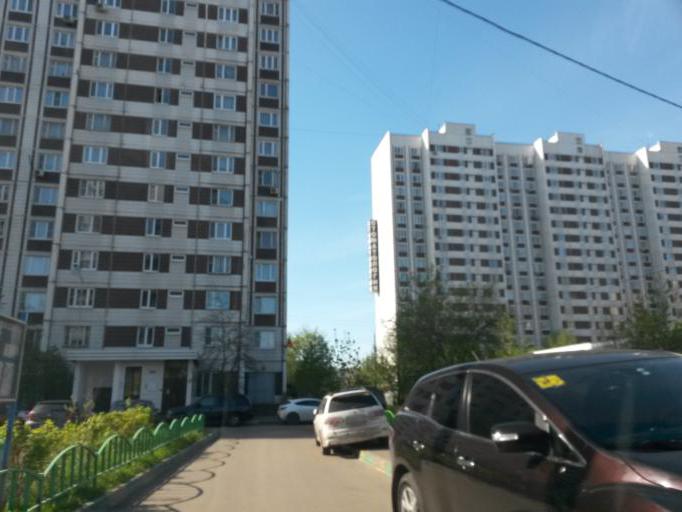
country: RU
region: Moscow
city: Mar'ino
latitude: 55.6422
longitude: 37.7385
